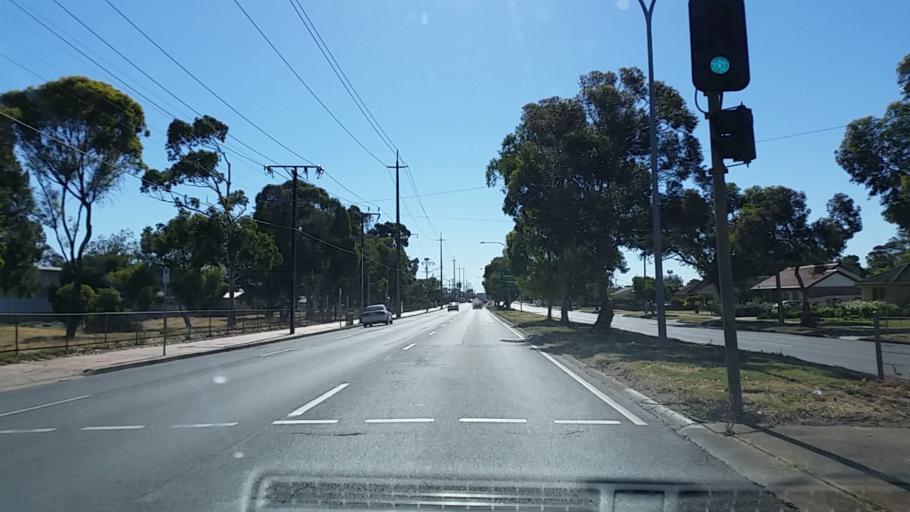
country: AU
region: South Australia
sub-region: Port Adelaide Enfield
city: Enfield
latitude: -34.8478
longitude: 138.6051
